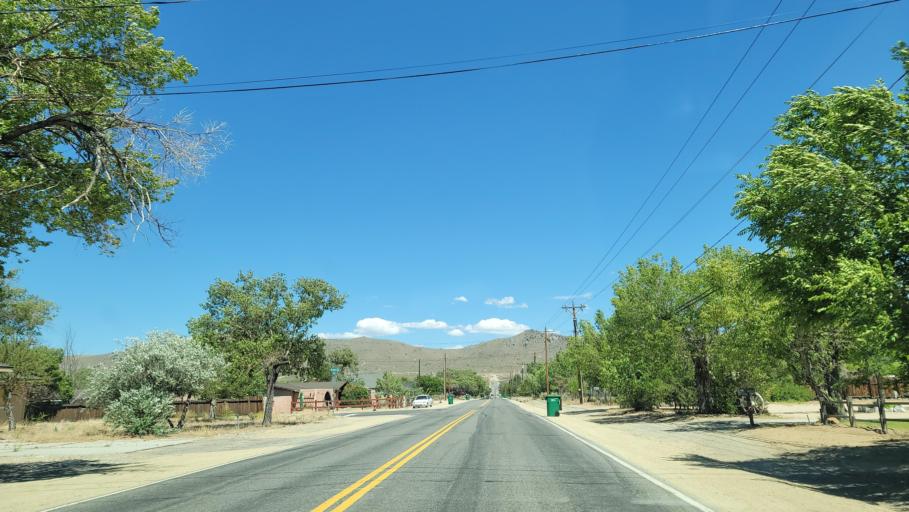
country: US
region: Nevada
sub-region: Carson City
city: Carson City
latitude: 39.1338
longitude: -119.7608
